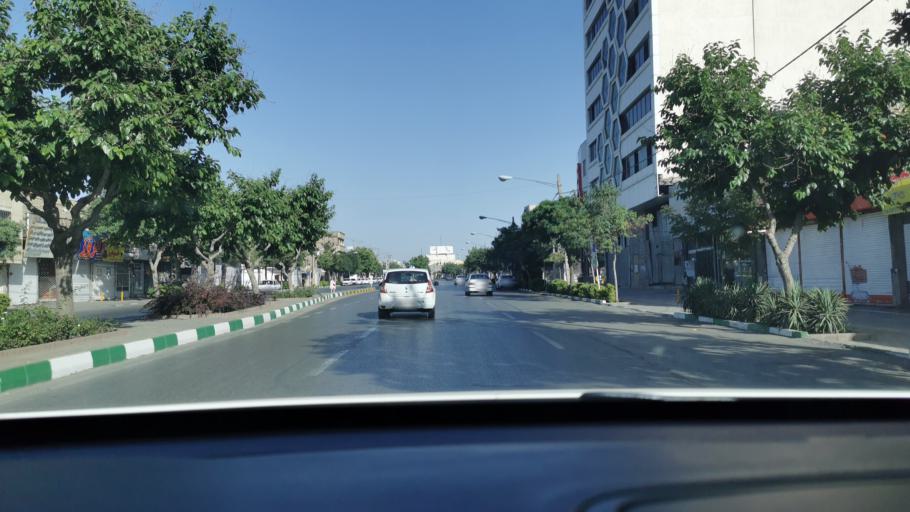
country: IR
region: Razavi Khorasan
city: Mashhad
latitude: 36.3328
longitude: 59.5147
